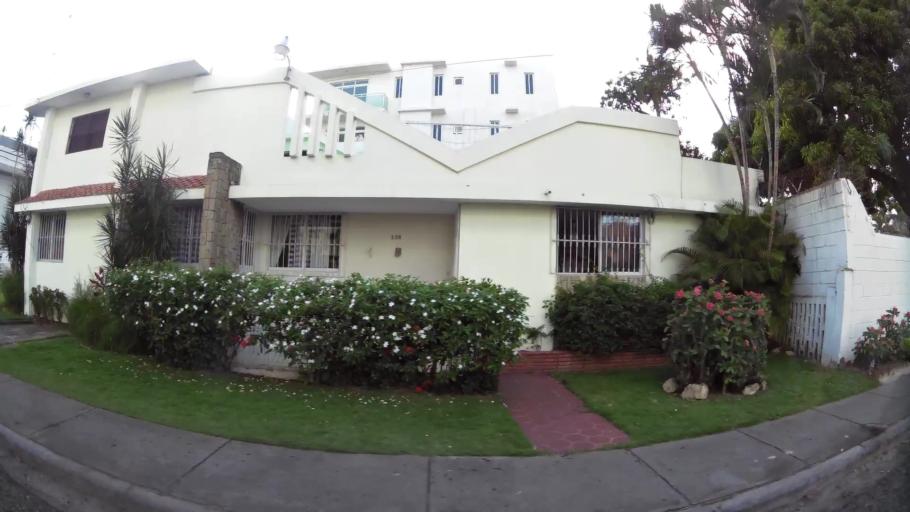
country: DO
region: Santiago
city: Santiago de los Caballeros
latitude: 19.4602
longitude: -70.6927
